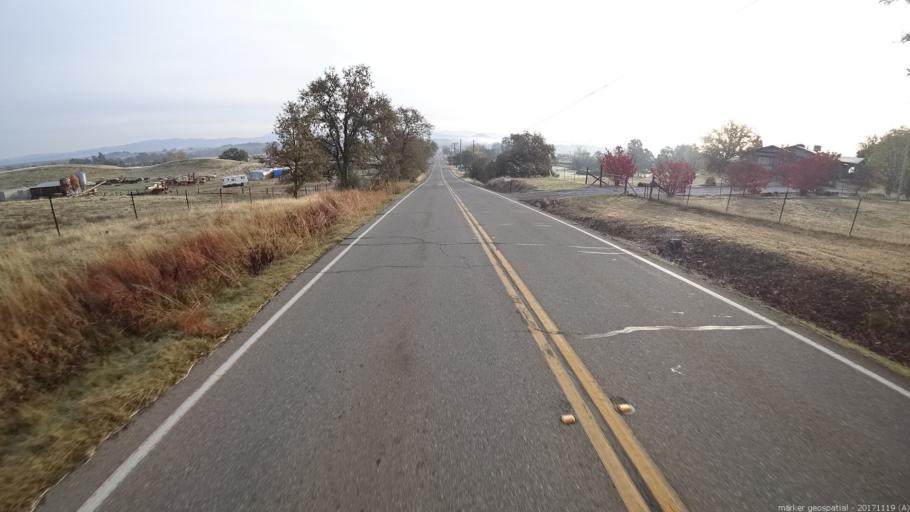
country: US
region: California
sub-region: Shasta County
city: Anderson
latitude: 40.4765
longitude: -122.2453
